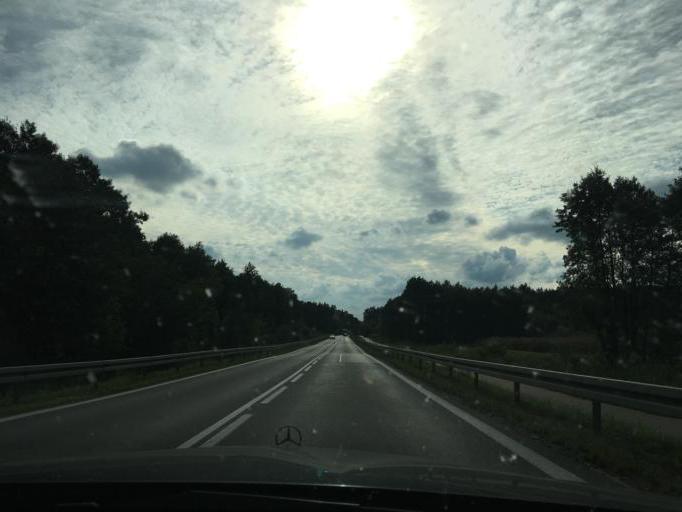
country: PL
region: Podlasie
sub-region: Powiat grajewski
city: Rajgrod
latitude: 53.7067
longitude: 22.6686
